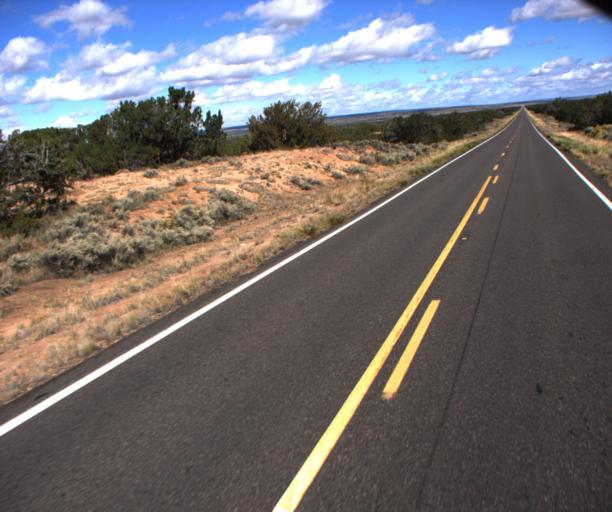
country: US
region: Arizona
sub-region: Apache County
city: Saint Johns
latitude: 34.8519
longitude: -109.2376
